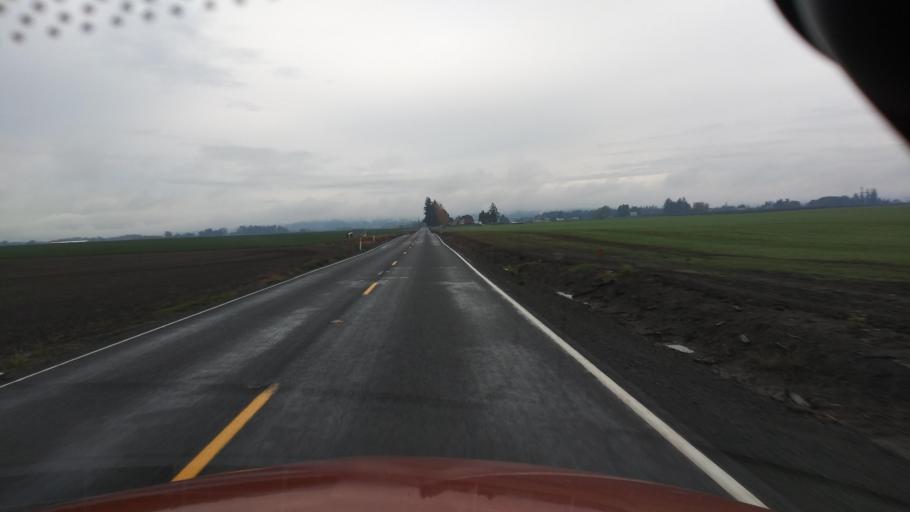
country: US
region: Oregon
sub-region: Washington County
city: North Plains
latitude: 45.5776
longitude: -123.0203
